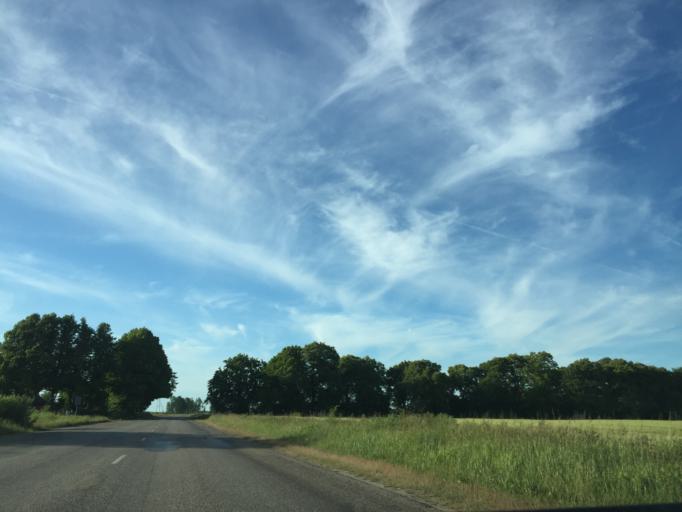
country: LV
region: Ventspils
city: Ventspils
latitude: 57.3301
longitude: 21.5640
